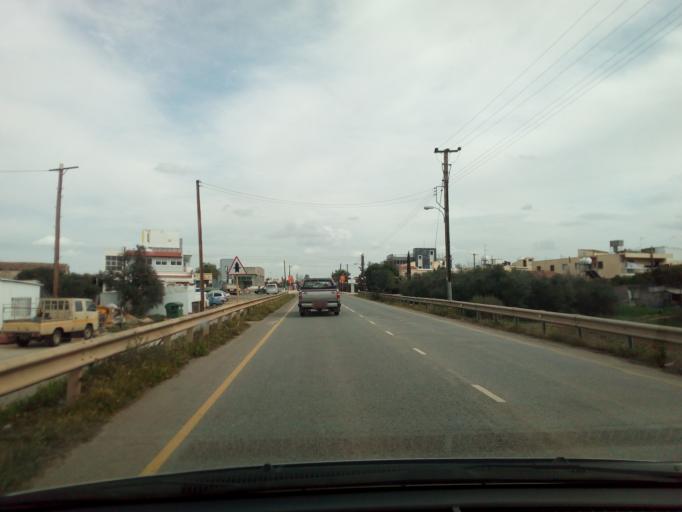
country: CY
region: Lefkosia
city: Akaki
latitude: 35.1364
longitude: 33.1258
